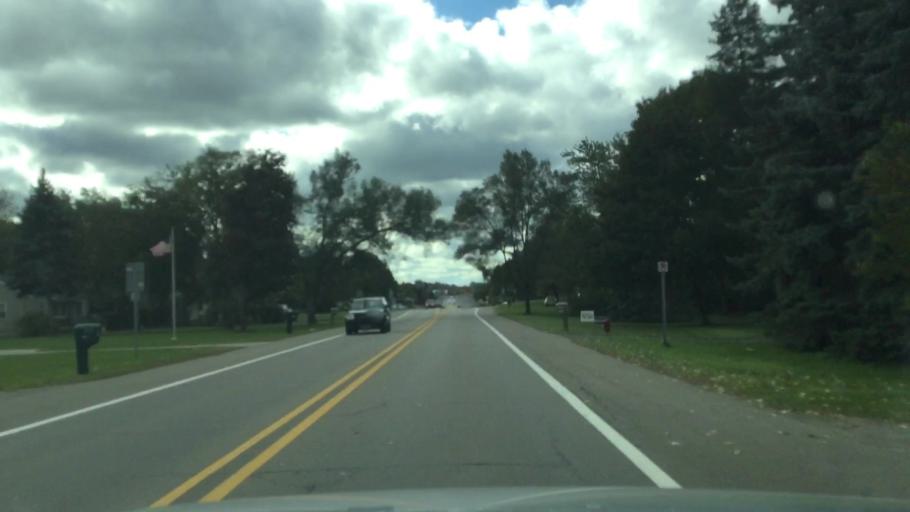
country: US
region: Michigan
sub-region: Oakland County
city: Clarkston
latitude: 42.7277
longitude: -83.4189
